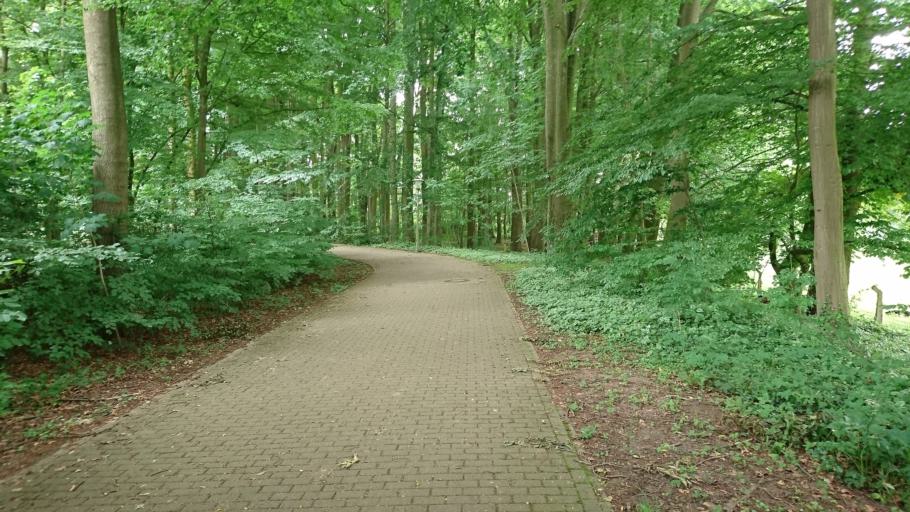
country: DE
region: Hamburg
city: Harburg
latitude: 53.4347
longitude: 9.9834
